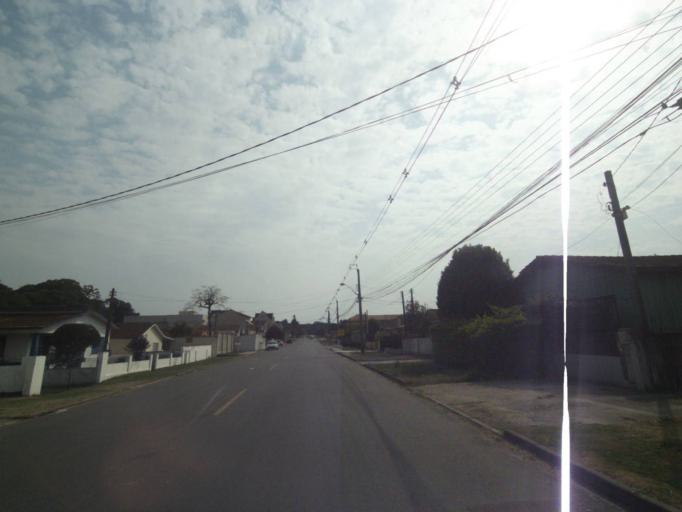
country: BR
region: Parana
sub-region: Sao Jose Dos Pinhais
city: Sao Jose dos Pinhais
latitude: -25.4930
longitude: -49.2084
